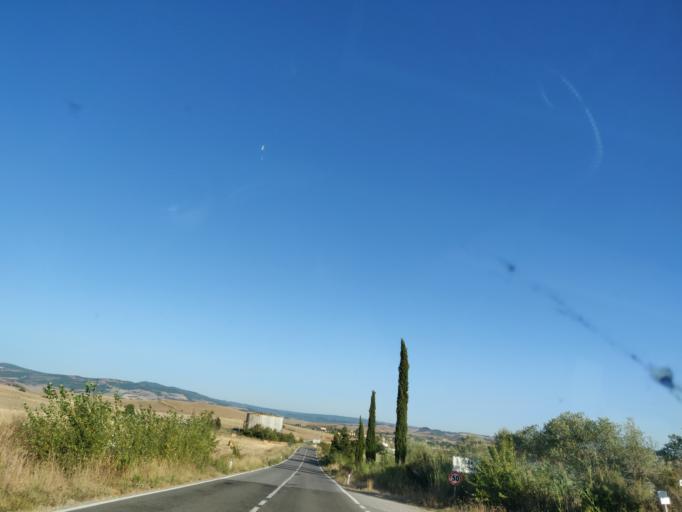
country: IT
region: Tuscany
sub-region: Provincia di Siena
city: Piancastagnaio
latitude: 42.8274
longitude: 11.7213
